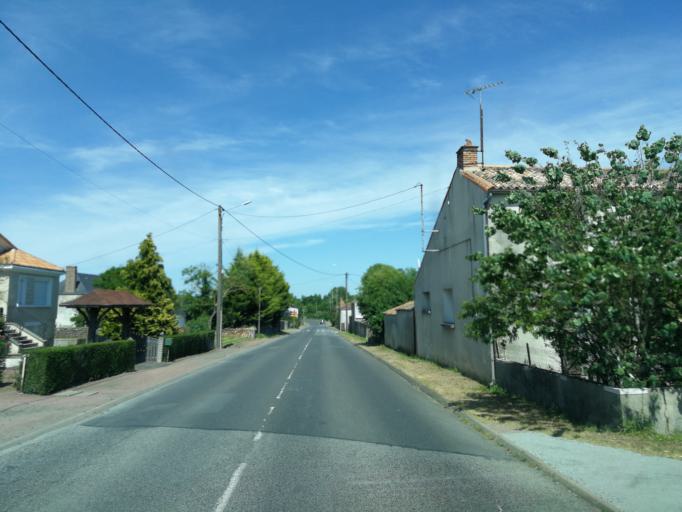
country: FR
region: Poitou-Charentes
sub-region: Departement des Deux-Sevres
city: Saint-Varent
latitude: 46.8985
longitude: -0.2908
